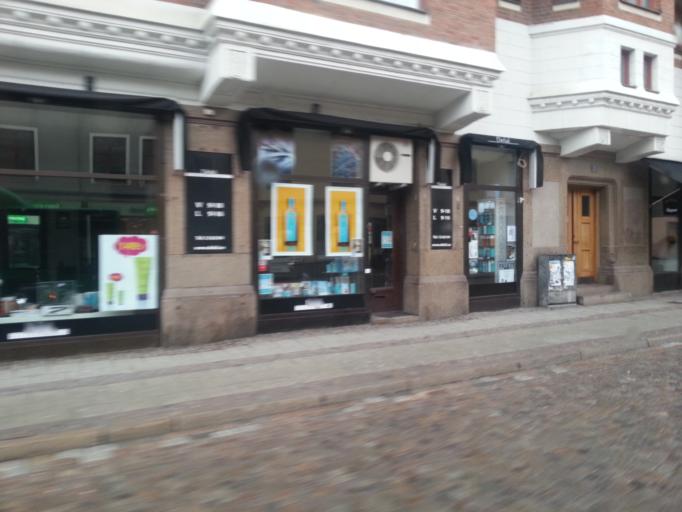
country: SE
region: Skane
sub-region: Lunds Kommun
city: Lund
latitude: 55.7016
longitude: 13.1929
